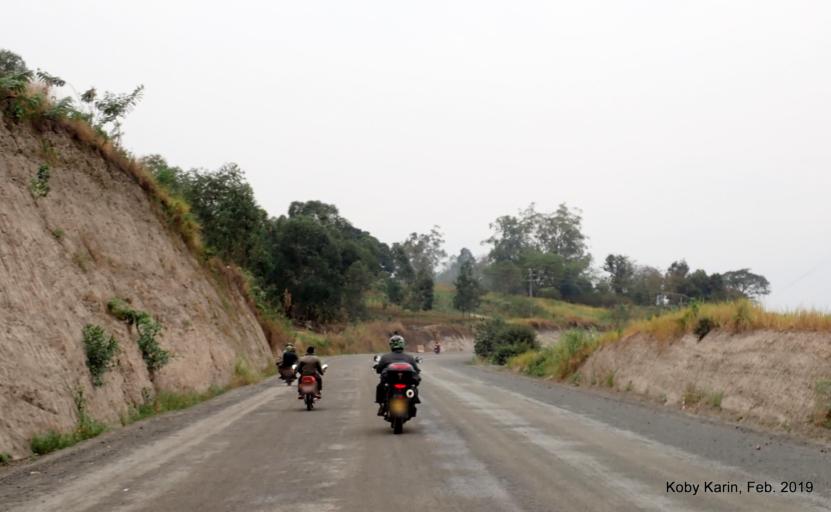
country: UG
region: Western Region
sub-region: Rubirizi District
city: Rubirizi
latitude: -0.2225
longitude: 30.0972
